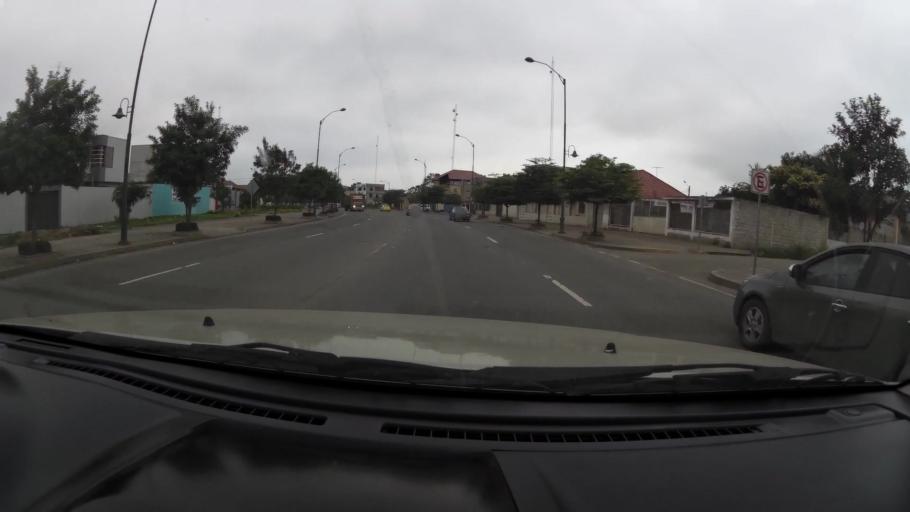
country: EC
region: El Oro
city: Machala
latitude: -3.2815
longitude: -79.9405
